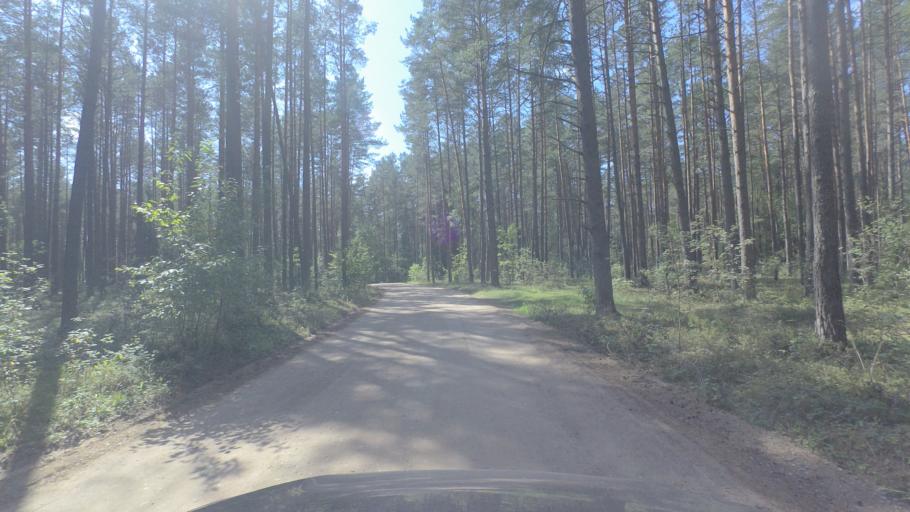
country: LT
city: Nemencine
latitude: 54.8477
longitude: 25.4985
